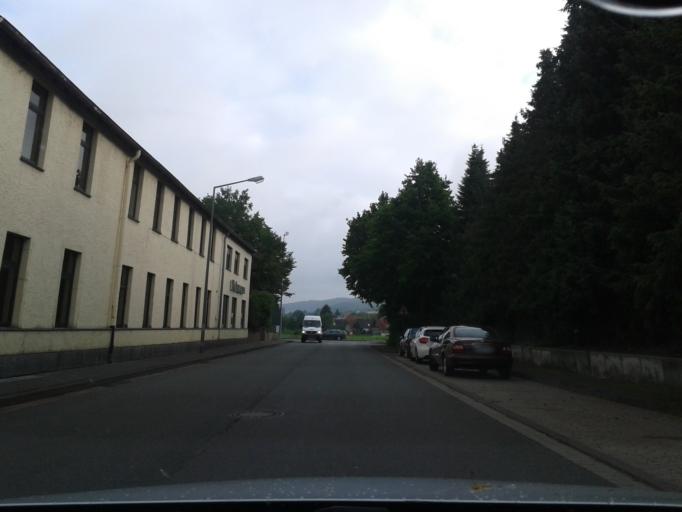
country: DE
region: North Rhine-Westphalia
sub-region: Regierungsbezirk Detmold
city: Barntrup
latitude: 51.9890
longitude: 9.1268
